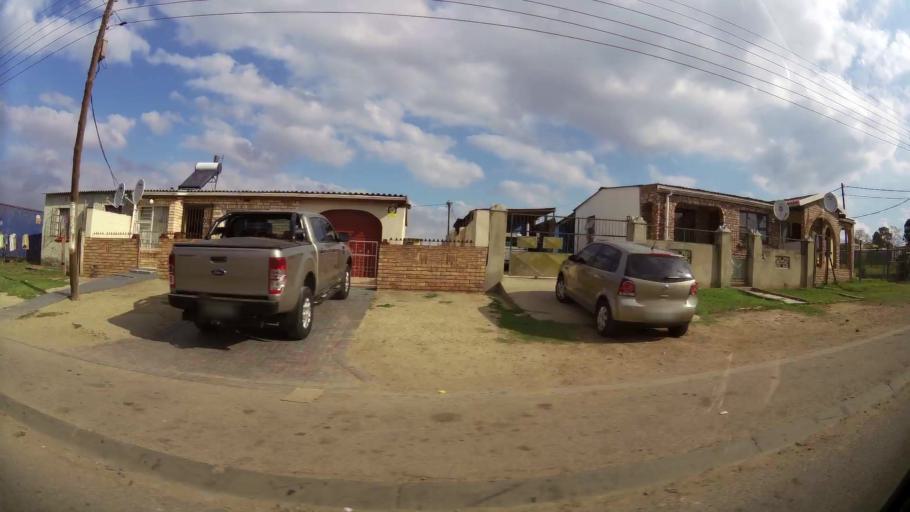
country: ZA
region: Eastern Cape
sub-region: Nelson Mandela Bay Metropolitan Municipality
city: Uitenhage
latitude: -33.7412
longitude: 25.3845
